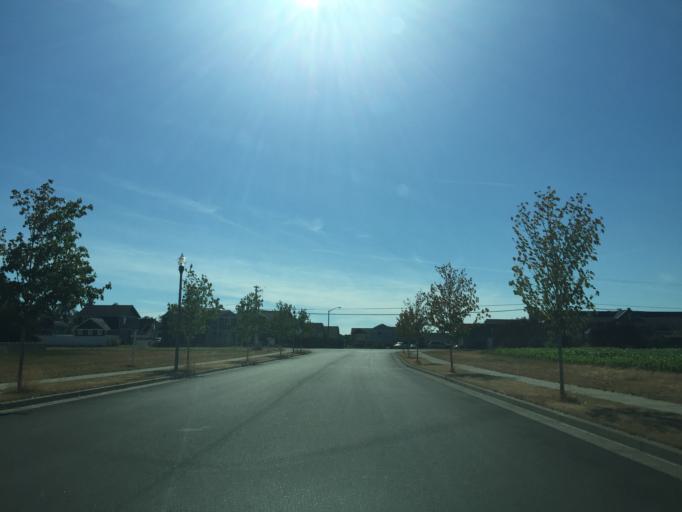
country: US
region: Washington
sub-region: Whatcom County
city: Lynden
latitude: 48.9618
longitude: -122.4173
